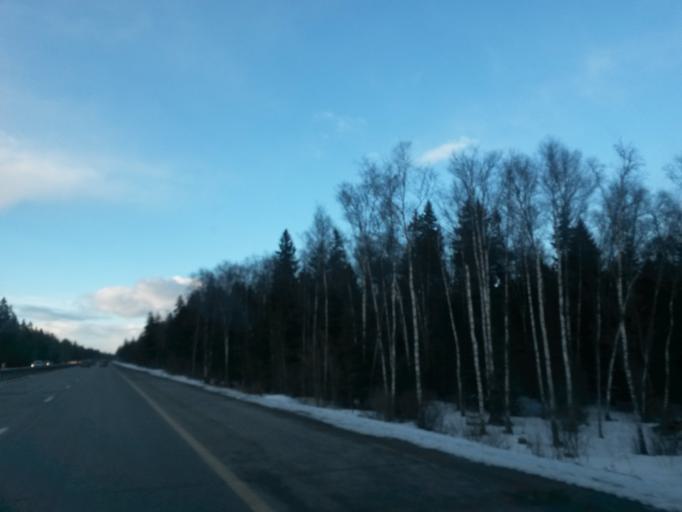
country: RU
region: Moskovskaya
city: Ashukino
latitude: 56.1603
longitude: 38.0140
